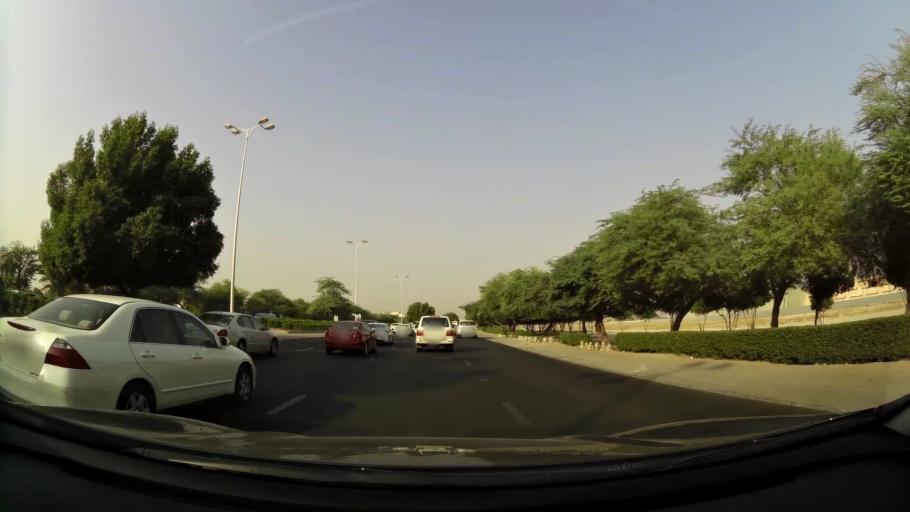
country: KW
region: Al Asimah
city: Ar Rabiyah
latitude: 29.3068
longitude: 47.9019
